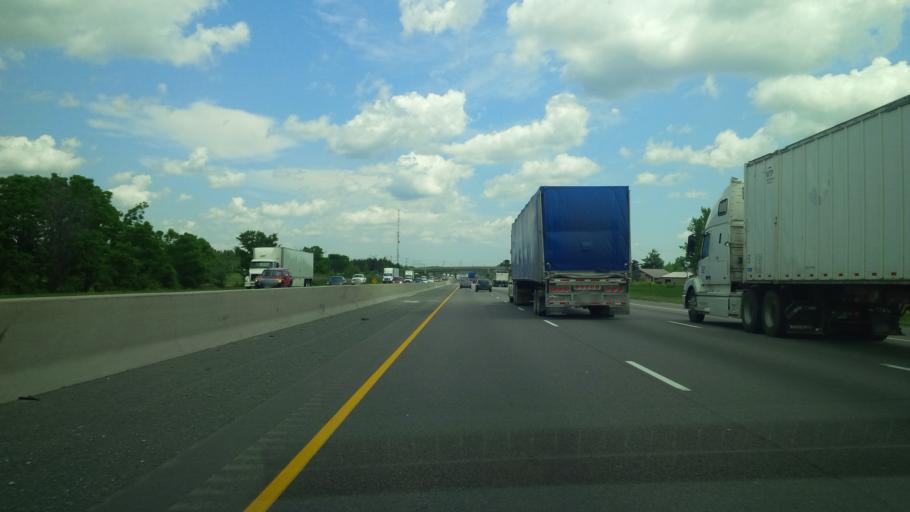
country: CA
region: Ontario
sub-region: Wellington County
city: Guelph
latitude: 43.4593
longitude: -80.1066
